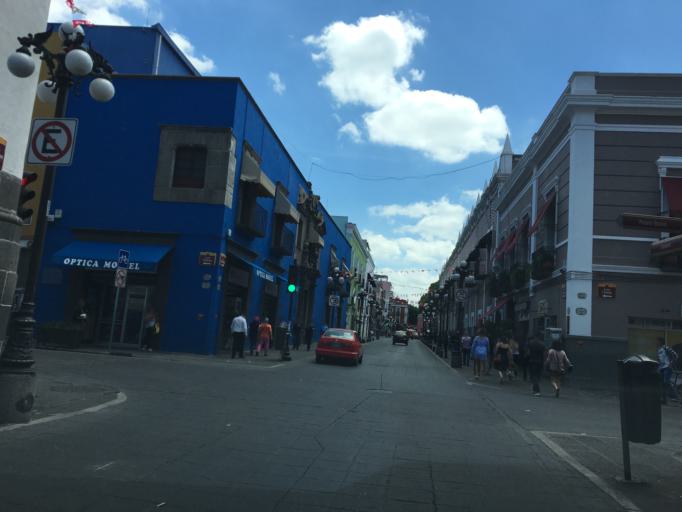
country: MX
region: Puebla
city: Puebla
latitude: 19.0421
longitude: -98.2000
